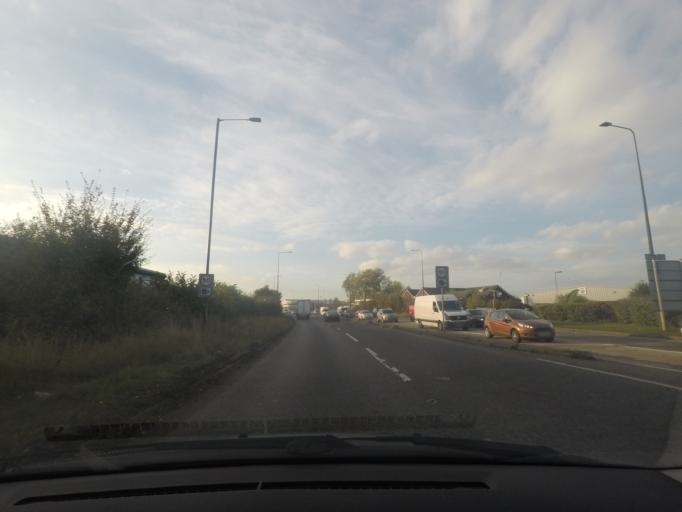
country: GB
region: England
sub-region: North East Lincolnshire
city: Grimbsy
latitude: 53.5755
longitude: -0.0973
